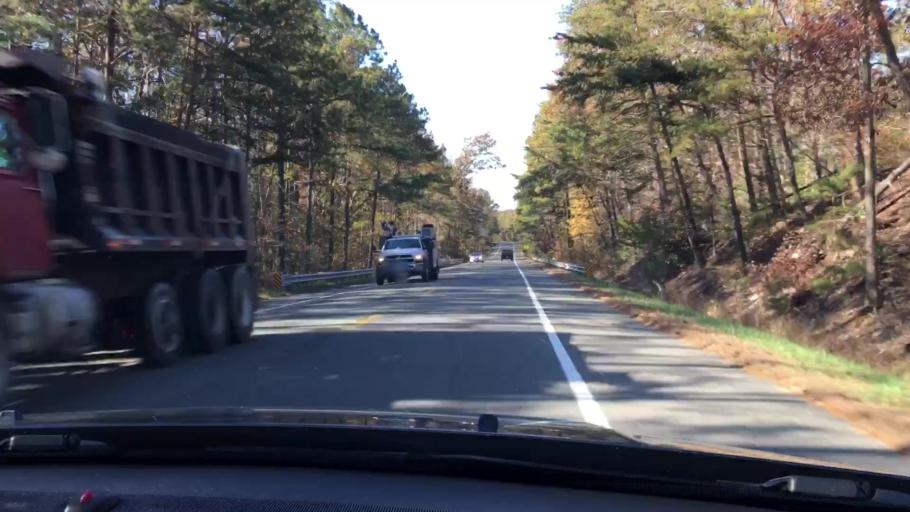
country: US
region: Virginia
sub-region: Hanover County
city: Hanover
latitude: 37.8389
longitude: -77.3780
